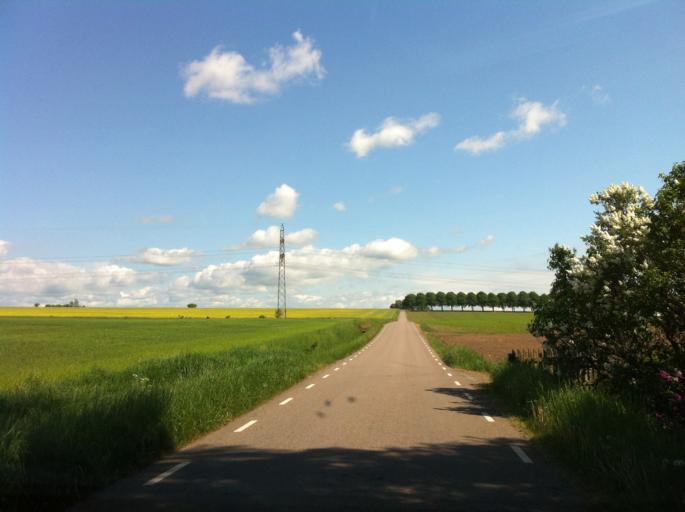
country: SE
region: Skane
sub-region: Helsingborg
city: Glumslov
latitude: 55.9627
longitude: 12.8801
